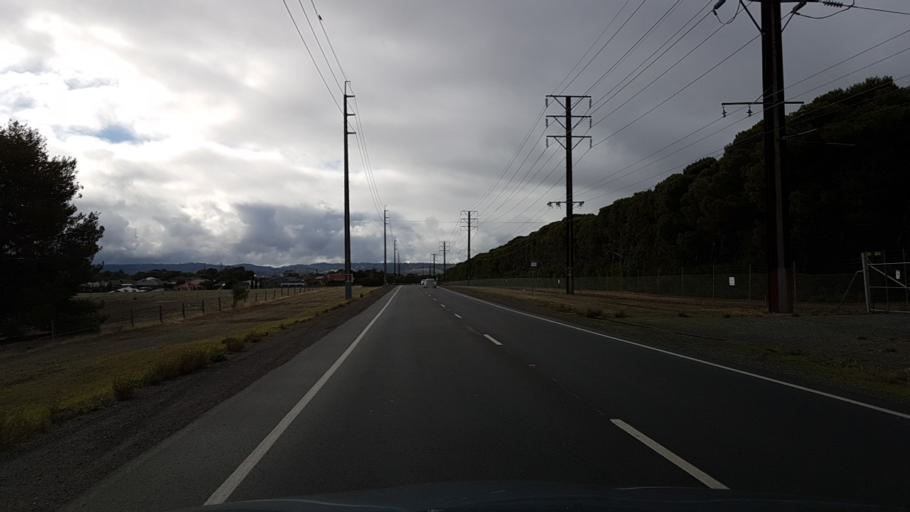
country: AU
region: South Australia
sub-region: Onkaparinga
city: Bedford Park
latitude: -35.0546
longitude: 138.5642
